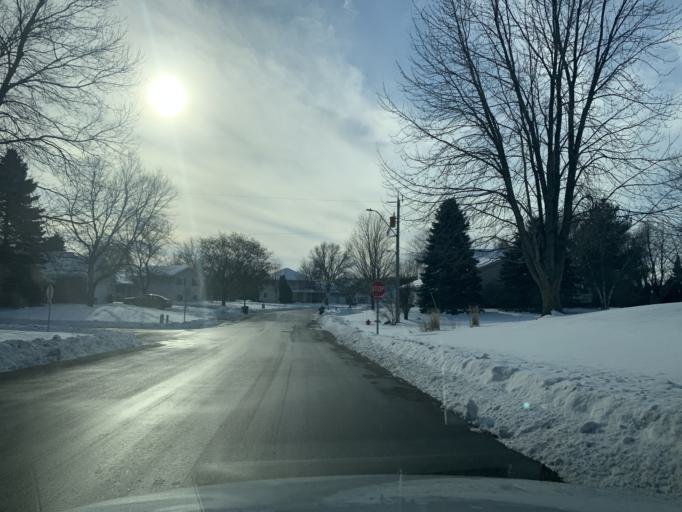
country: US
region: Minnesota
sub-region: Wright County
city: Saint Michael
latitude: 45.2065
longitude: -93.6553
